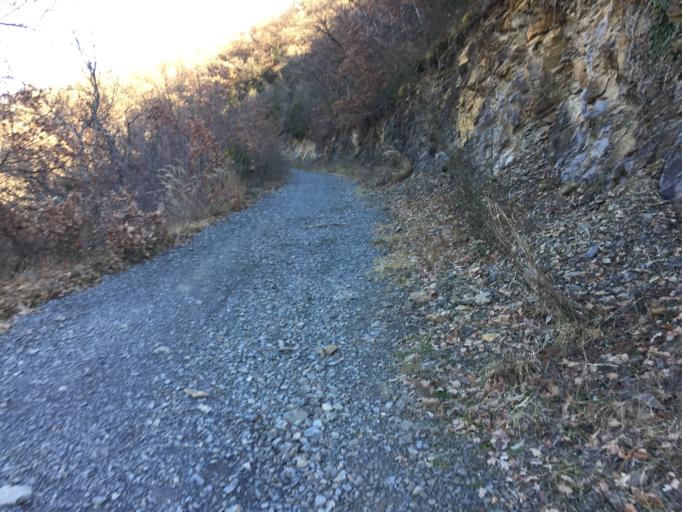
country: FR
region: Provence-Alpes-Cote d'Azur
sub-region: Departement des Alpes-de-Haute-Provence
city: Digne-les-Bains
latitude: 44.0768
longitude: 6.2700
